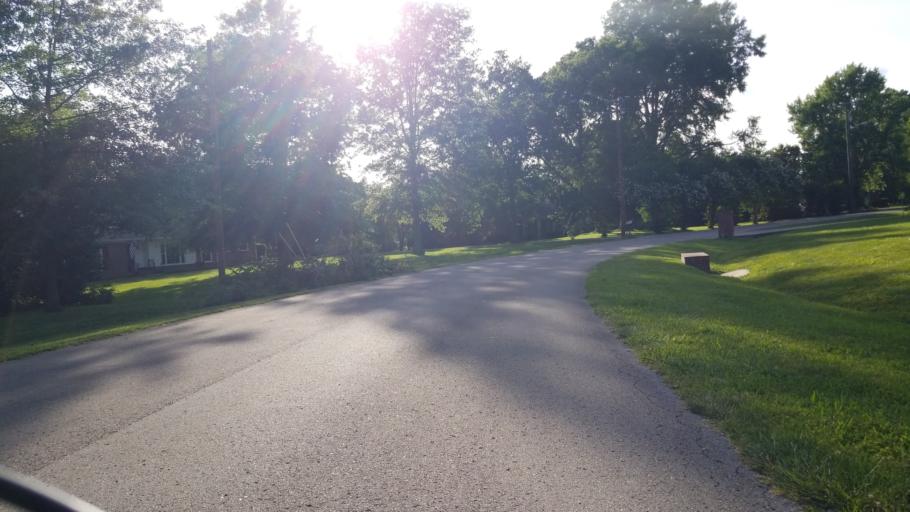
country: US
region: Tennessee
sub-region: Davidson County
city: Forest Hills
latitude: 36.0422
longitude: -86.8550
